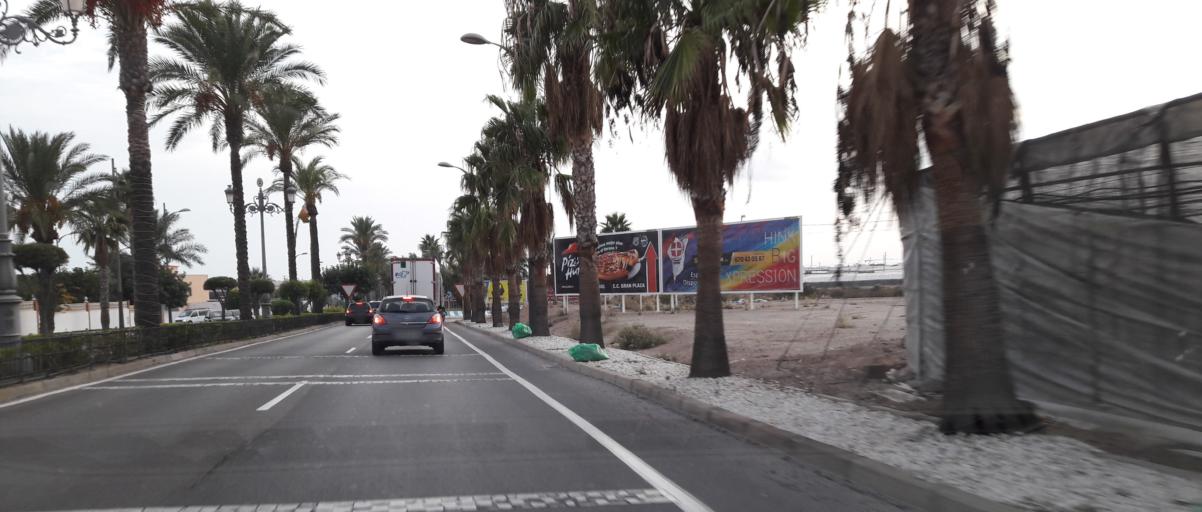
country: ES
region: Andalusia
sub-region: Provincia de Almeria
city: Roquetas de Mar
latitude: 36.7932
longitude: -2.6041
